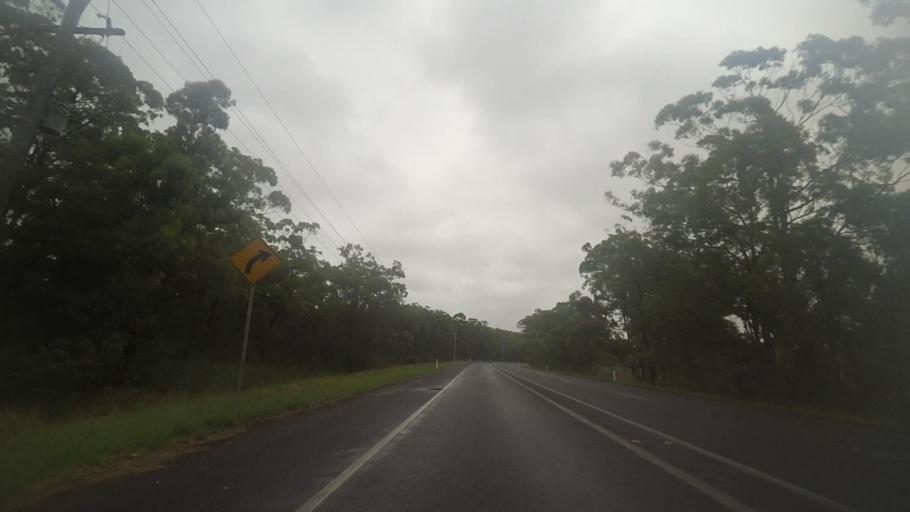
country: AU
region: New South Wales
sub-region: Port Stephens Shire
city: Port Stephens
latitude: -32.6466
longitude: 151.9808
